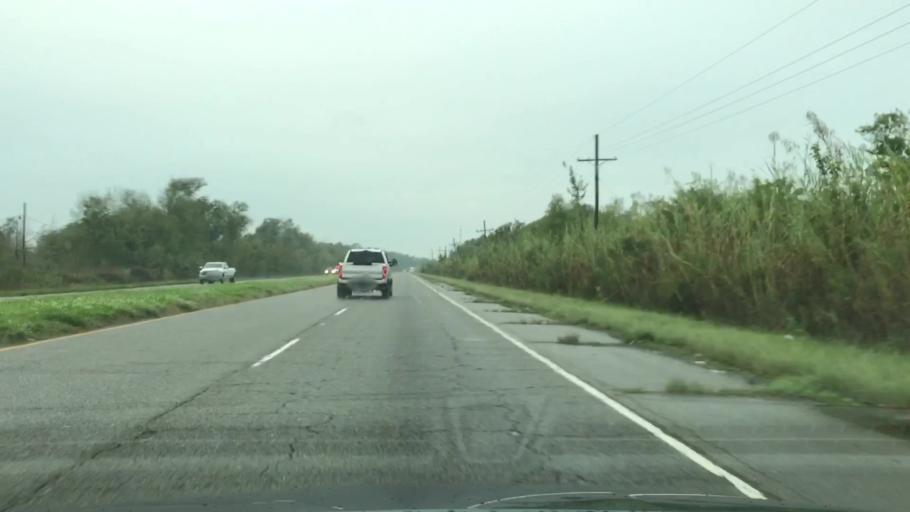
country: US
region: Louisiana
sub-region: Saint Charles Parish
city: Des Allemands
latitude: 29.7934
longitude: -90.5106
